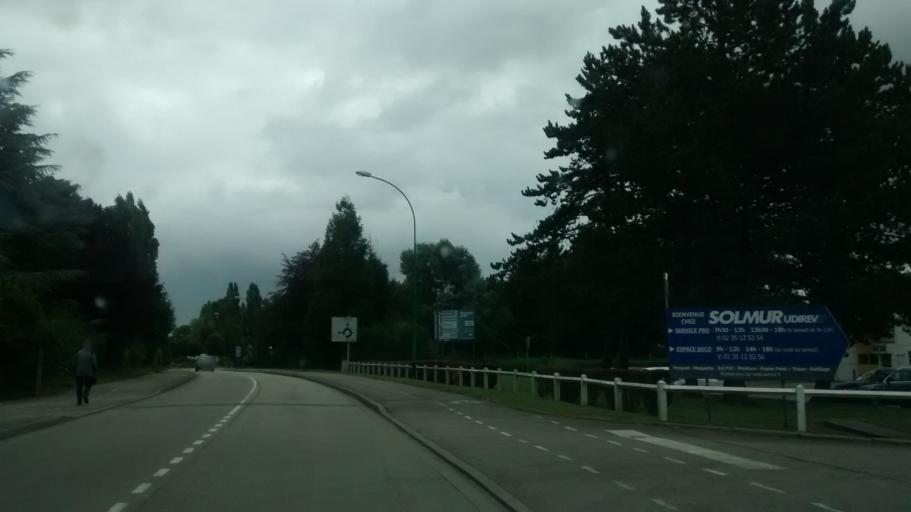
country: FR
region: Haute-Normandie
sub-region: Departement de la Seine-Maritime
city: Bois-Guillaume
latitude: 49.4670
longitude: 1.1386
